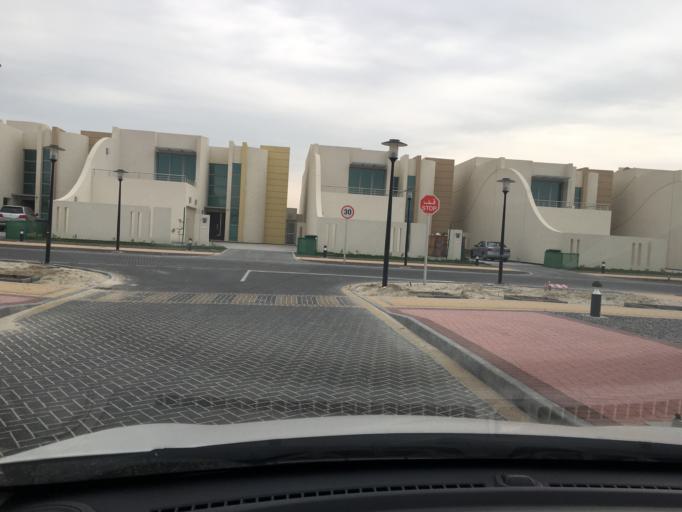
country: BH
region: Central Governorate
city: Dar Kulayb
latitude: 25.8288
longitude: 50.6050
